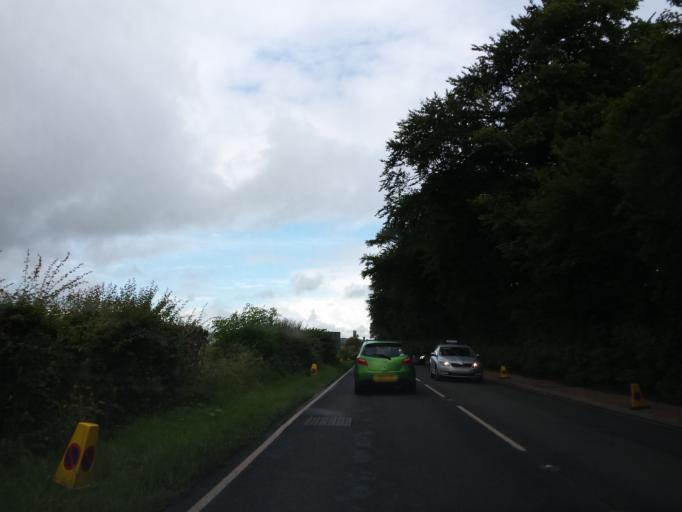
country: GB
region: Scotland
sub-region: Fife
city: Leuchars
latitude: 56.3594
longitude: -2.8953
